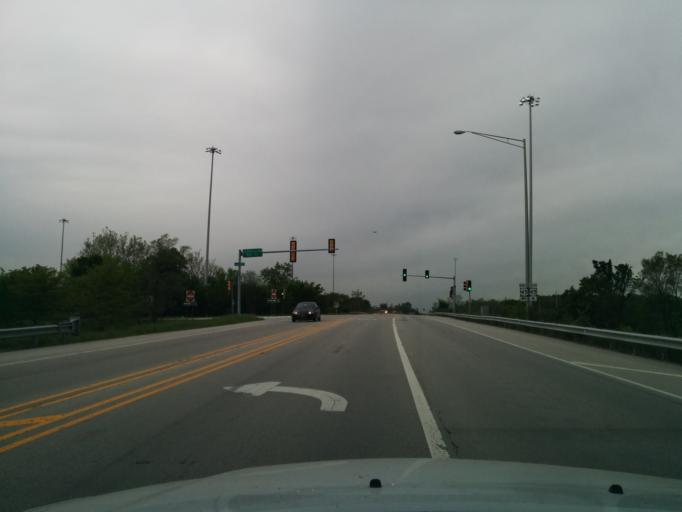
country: US
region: Illinois
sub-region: Cook County
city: Palos Park
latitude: 41.6830
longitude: -87.8531
